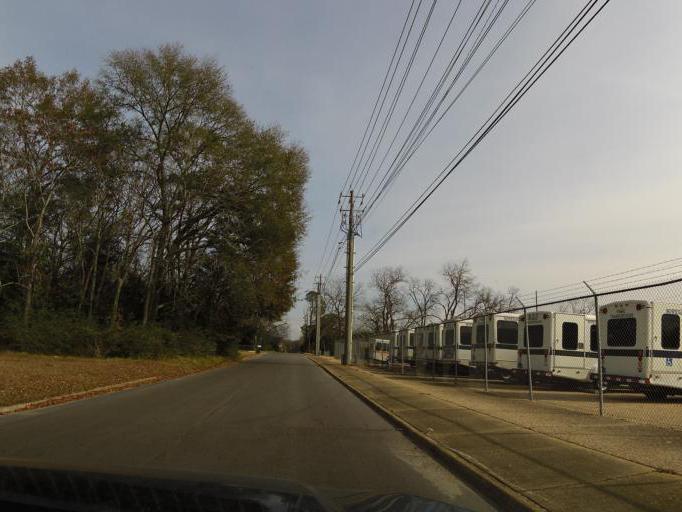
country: US
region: Alabama
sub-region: Houston County
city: Dothan
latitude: 31.2265
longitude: -85.3868
